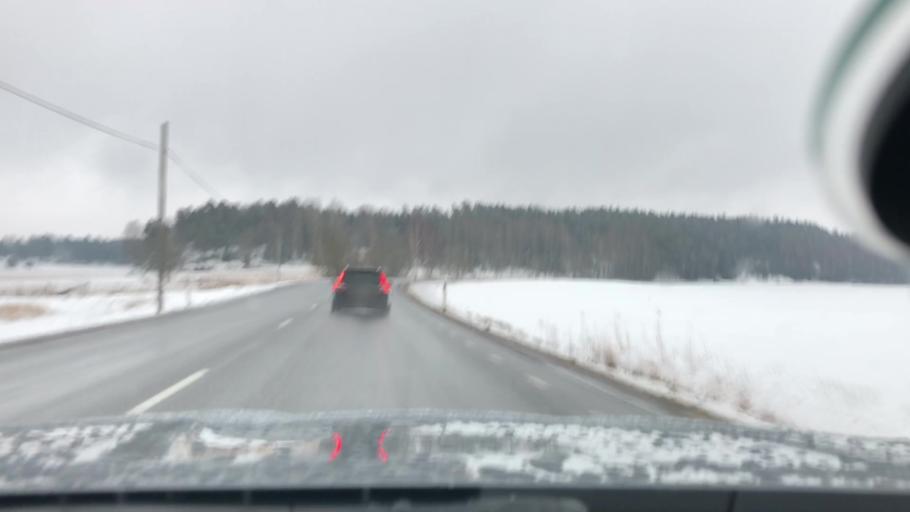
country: SE
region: Stockholm
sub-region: Sodertalje Kommun
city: Pershagen
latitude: 59.0610
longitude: 17.6112
